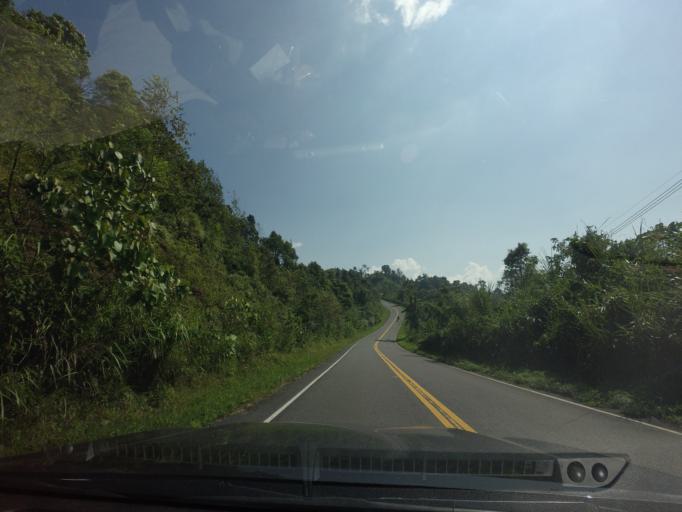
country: TH
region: Nan
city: Bo Kluea
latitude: 19.0500
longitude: 101.0908
